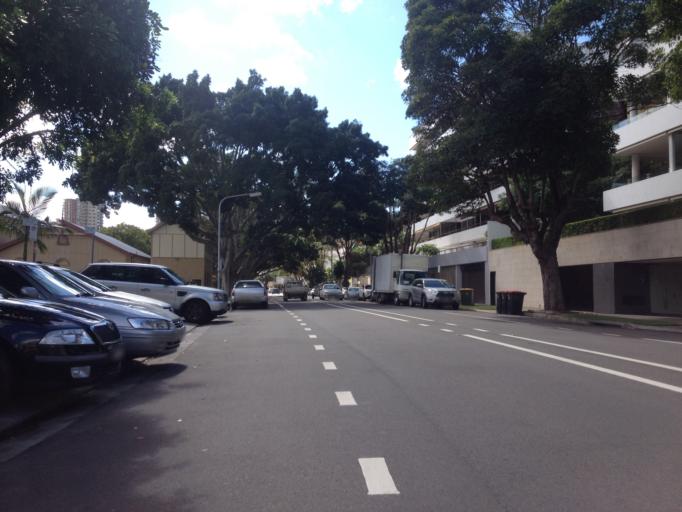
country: AU
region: New South Wales
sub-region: Woollahra
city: Darling Point
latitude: -33.8738
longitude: 151.2346
